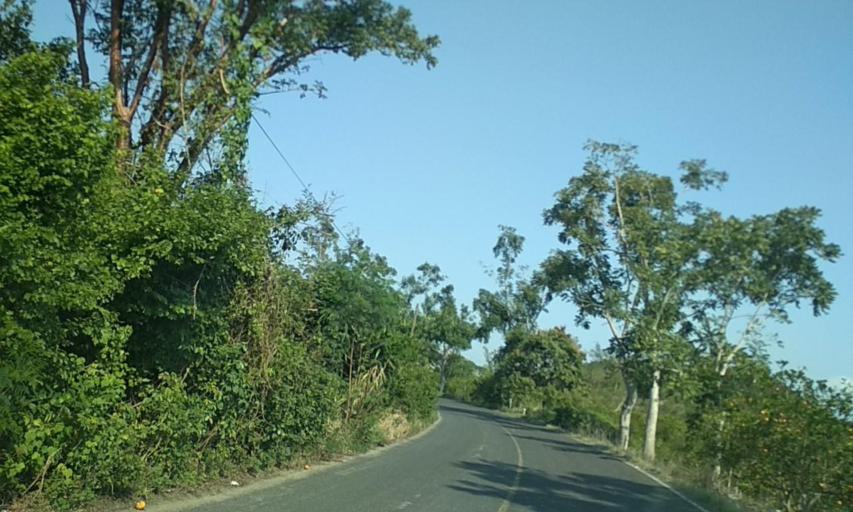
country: MX
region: Veracruz
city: Gutierrez Zamora
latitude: 20.3470
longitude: -97.1483
